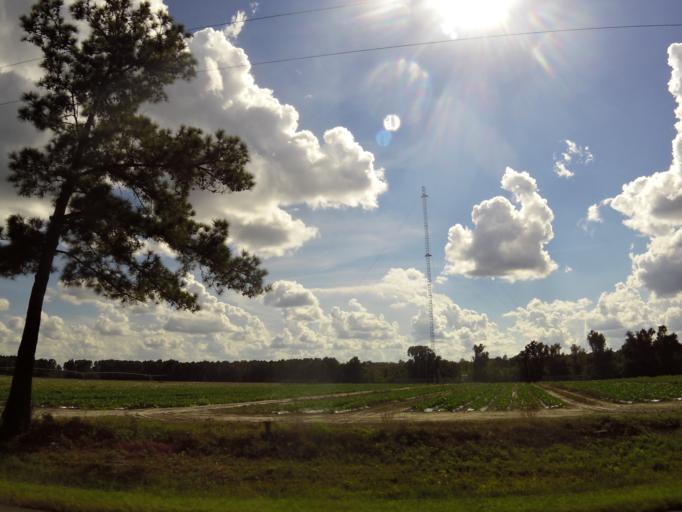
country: US
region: Georgia
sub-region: Echols County
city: Statenville
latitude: 30.7666
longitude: -83.1314
